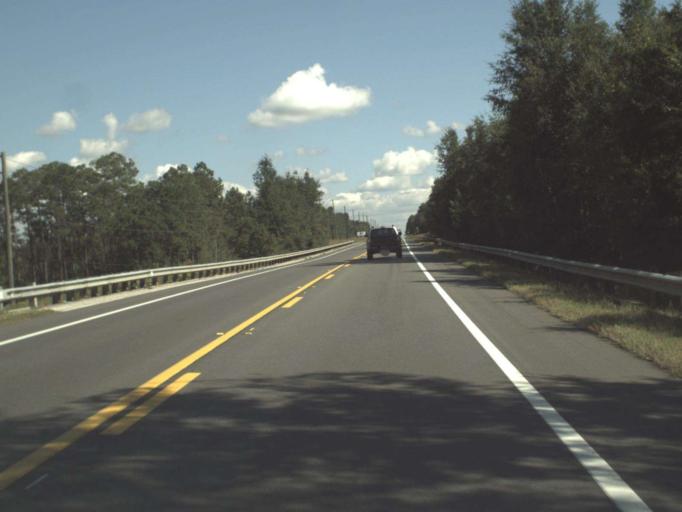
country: US
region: Florida
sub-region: Walton County
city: Freeport
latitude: 30.5118
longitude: -86.1768
